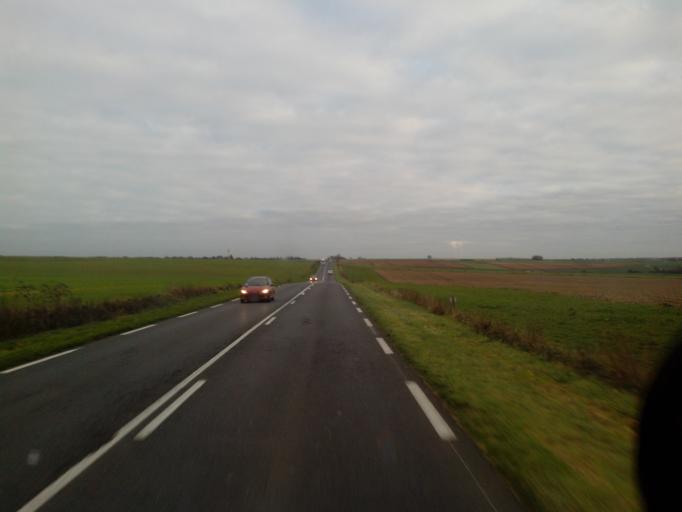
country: FR
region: Poitou-Charentes
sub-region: Departement de la Vienne
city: Cisse
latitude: 46.6396
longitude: 0.2076
